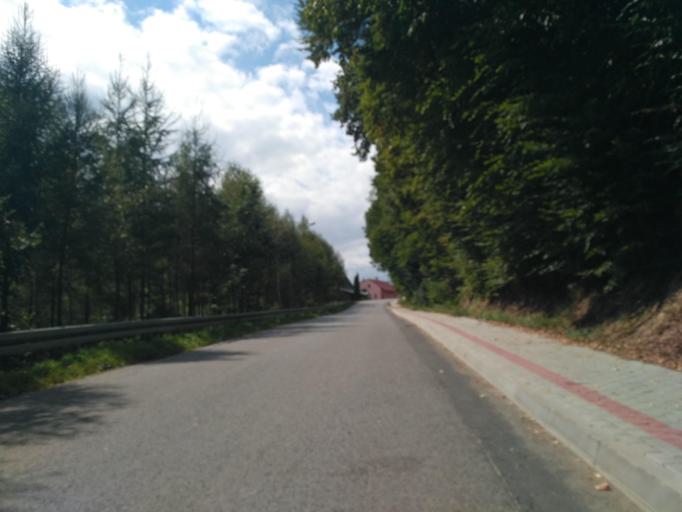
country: PL
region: Subcarpathian Voivodeship
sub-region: Powiat rzeszowski
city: Dynow
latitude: 49.8140
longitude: 22.2702
